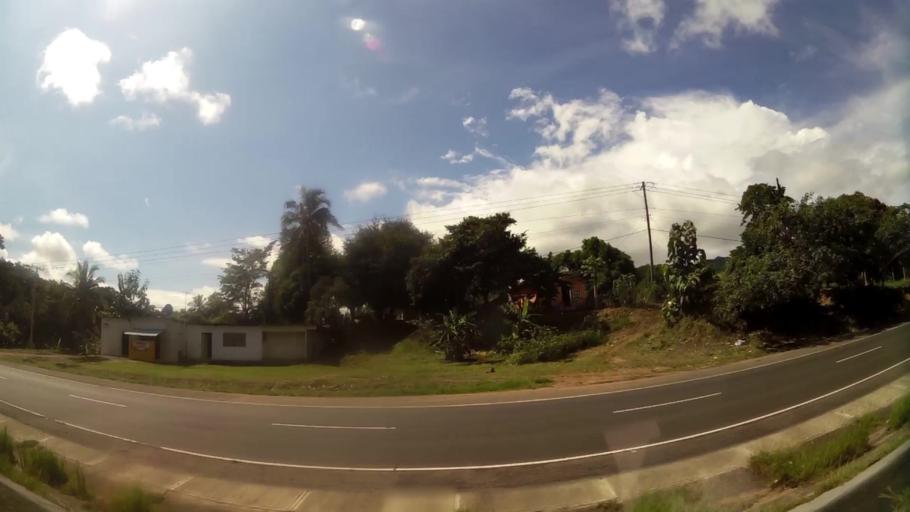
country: PA
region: Panama
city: Bejuco
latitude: 8.6364
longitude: -79.8810
